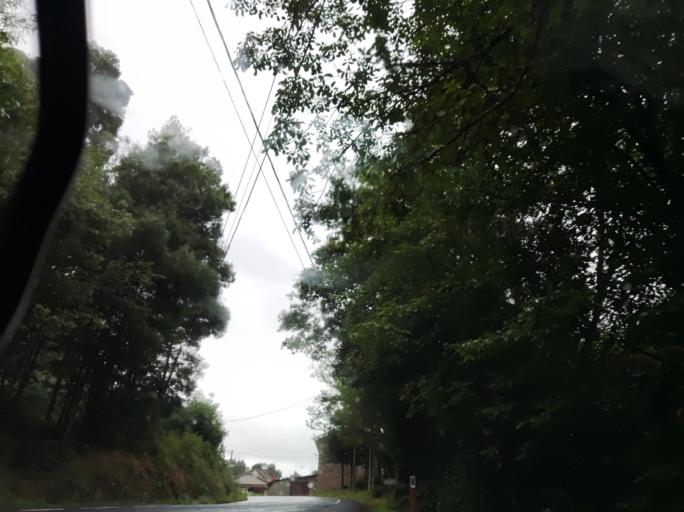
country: ES
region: Galicia
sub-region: Provincia da Coruna
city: Rianxo
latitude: 42.6972
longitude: -8.8408
